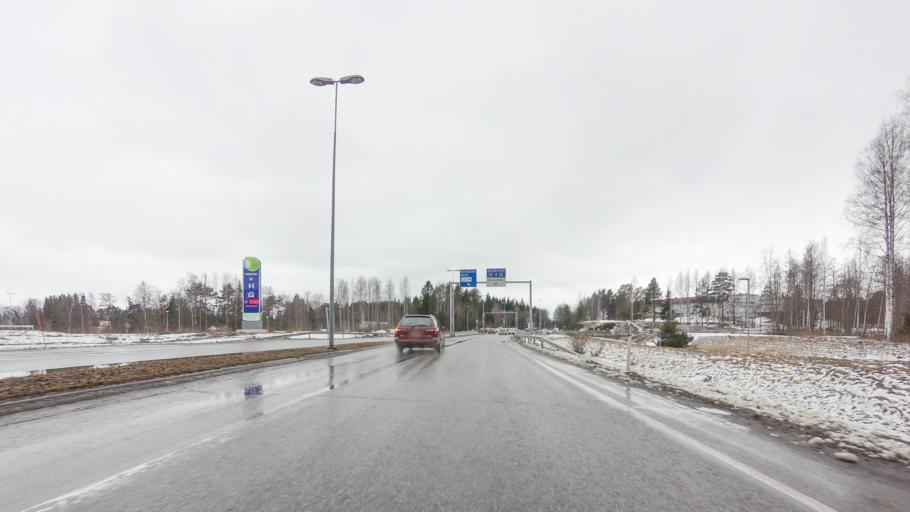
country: FI
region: Southern Savonia
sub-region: Savonlinna
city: Savonlinna
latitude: 61.8669
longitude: 28.9401
